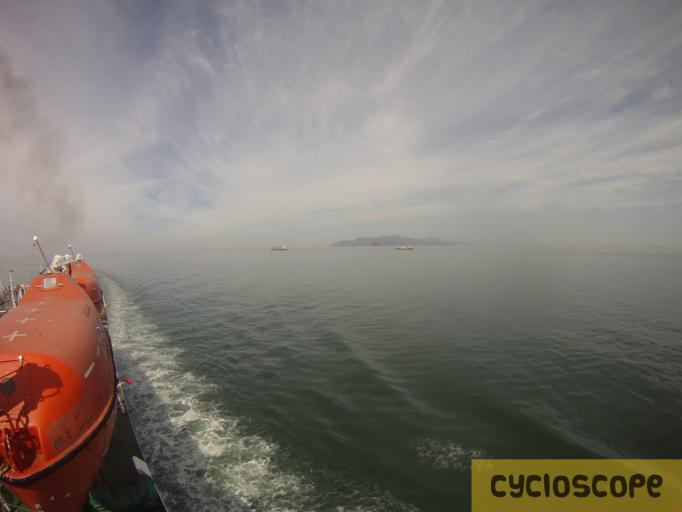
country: KR
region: Incheon
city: Incheon
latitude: 37.3428
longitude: 126.4962
